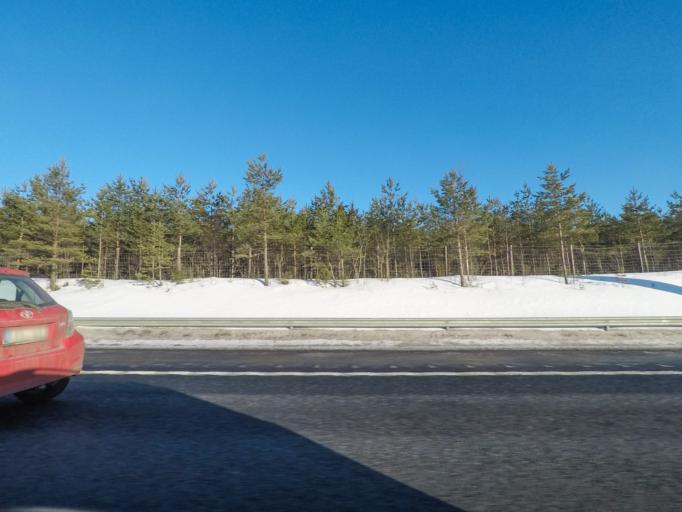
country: FI
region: Paijanne Tavastia
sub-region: Lahti
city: Nastola
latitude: 61.1055
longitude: 25.9151
